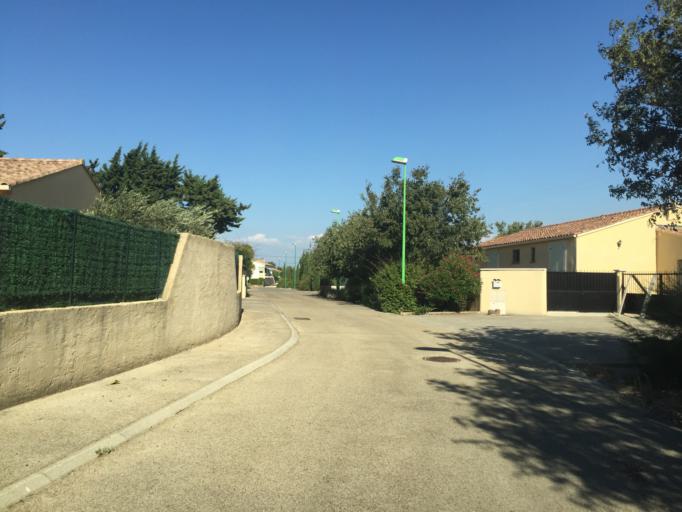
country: FR
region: Provence-Alpes-Cote d'Azur
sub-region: Departement du Vaucluse
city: Sorgues
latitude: 44.0222
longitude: 4.8618
